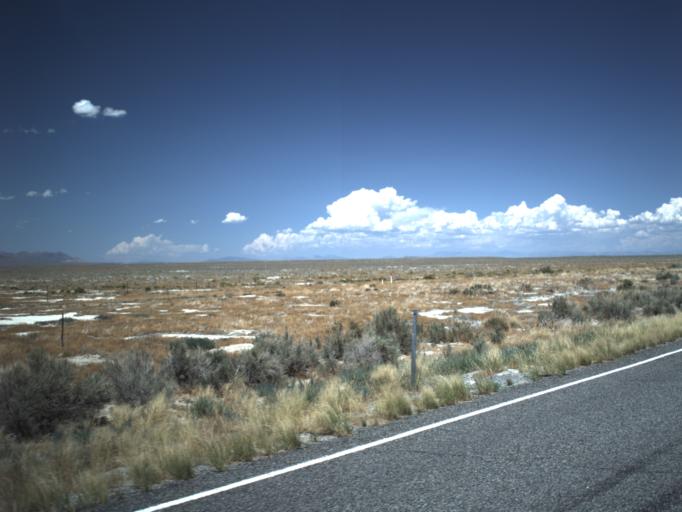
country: US
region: Utah
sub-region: Millard County
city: Delta
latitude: 39.2118
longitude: -112.9636
